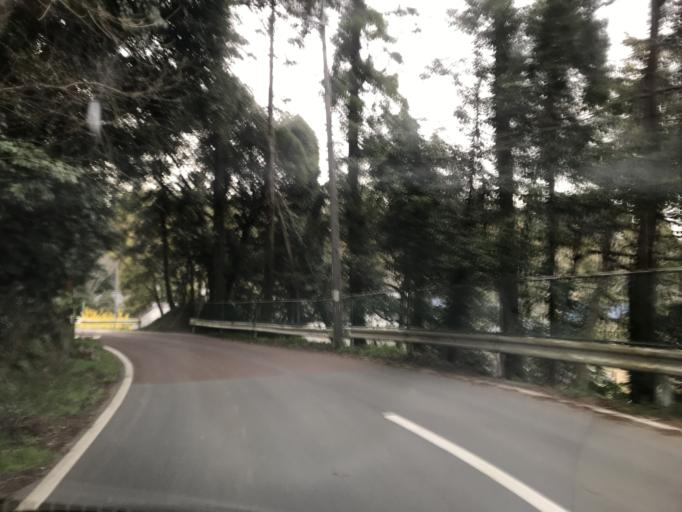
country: JP
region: Chiba
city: Omigawa
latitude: 35.7976
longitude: 140.5967
